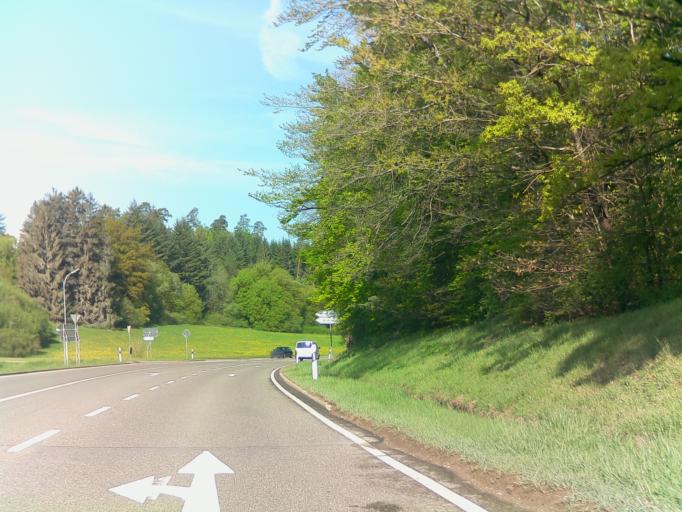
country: DE
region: Baden-Wuerttemberg
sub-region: Regierungsbezirk Stuttgart
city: Motzingen
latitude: 48.5425
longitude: 8.7561
